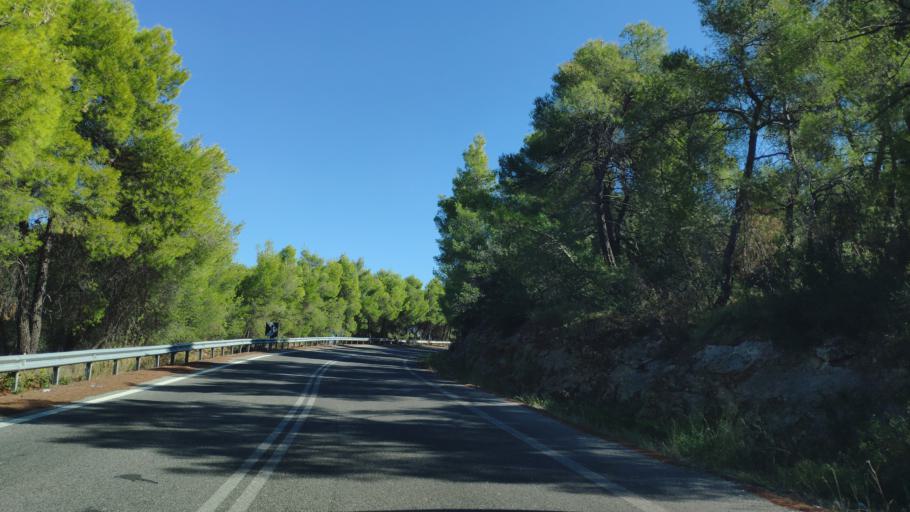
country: GR
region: Peloponnese
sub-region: Nomos Korinthias
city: Sofikon
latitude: 37.8290
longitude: 23.0317
